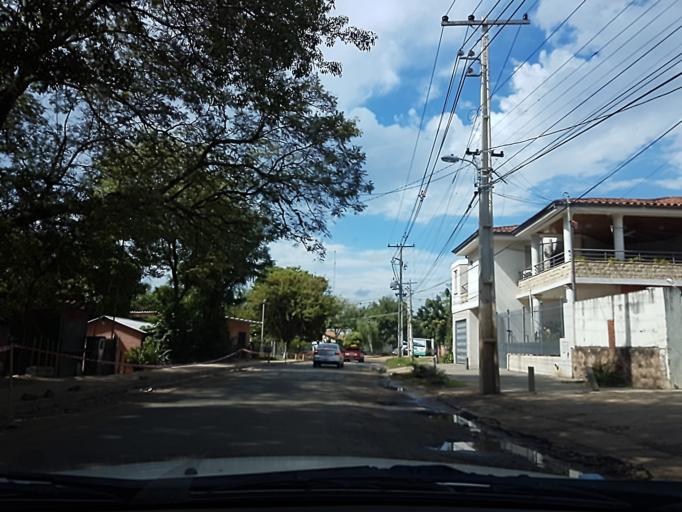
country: PY
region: Central
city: Colonia Mariano Roque Alonso
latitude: -25.2342
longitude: -57.5732
